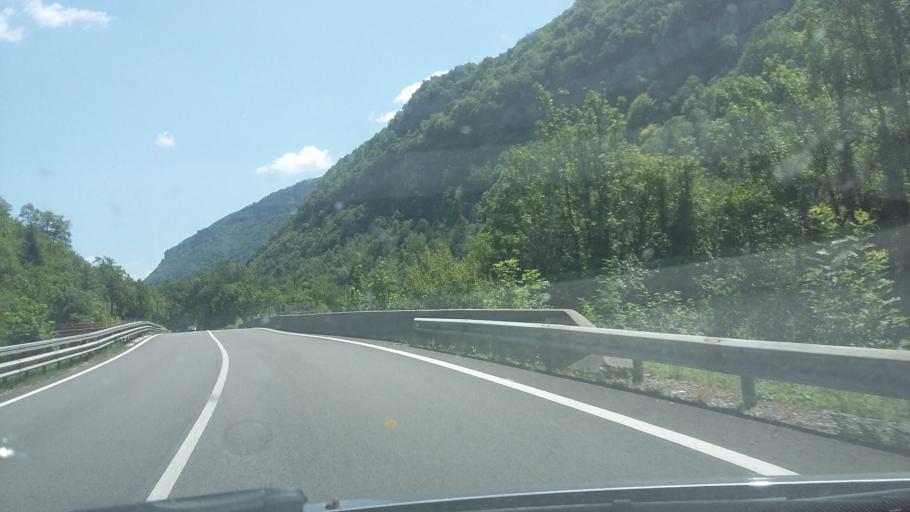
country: FR
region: Rhone-Alpes
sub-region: Departement de l'Ain
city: Tenay
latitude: 45.8528
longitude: 5.5442
